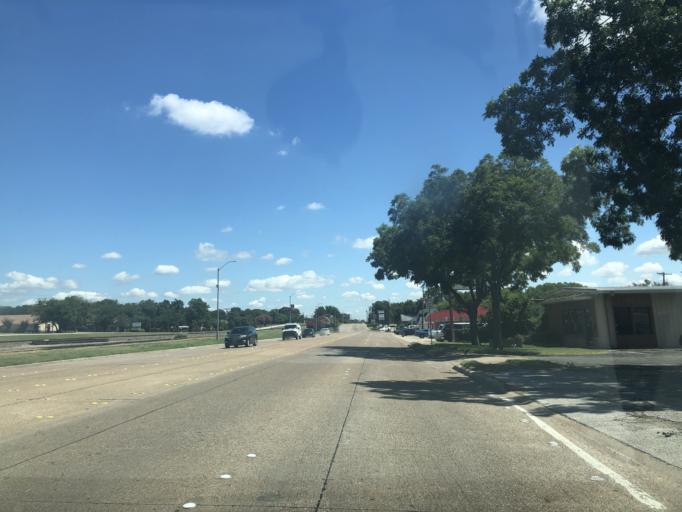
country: US
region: Texas
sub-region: Dallas County
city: Duncanville
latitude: 32.6551
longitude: -96.9080
